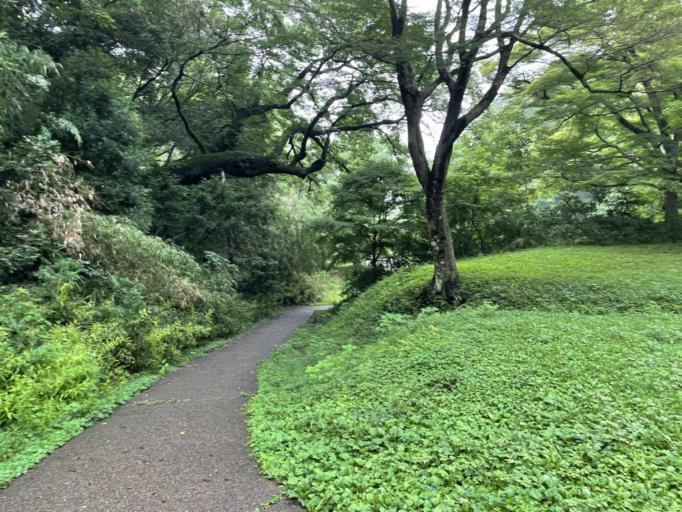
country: JP
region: Chiba
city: Sakura
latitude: 35.7219
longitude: 140.2184
